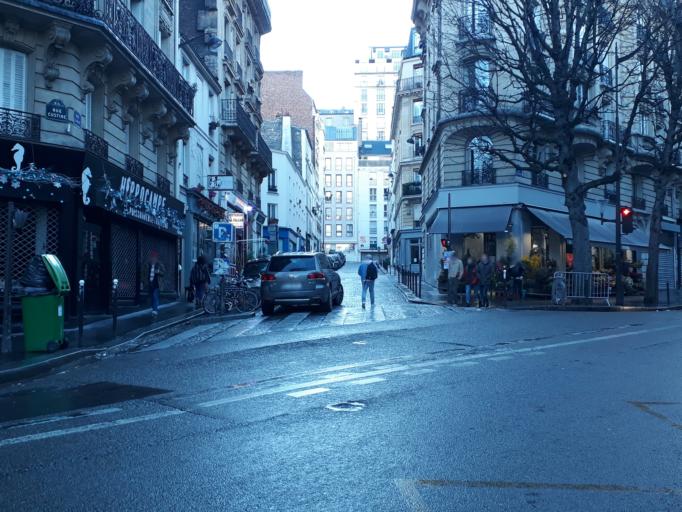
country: FR
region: Ile-de-France
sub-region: Paris
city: Saint-Ouen
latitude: 48.8889
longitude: 2.3463
